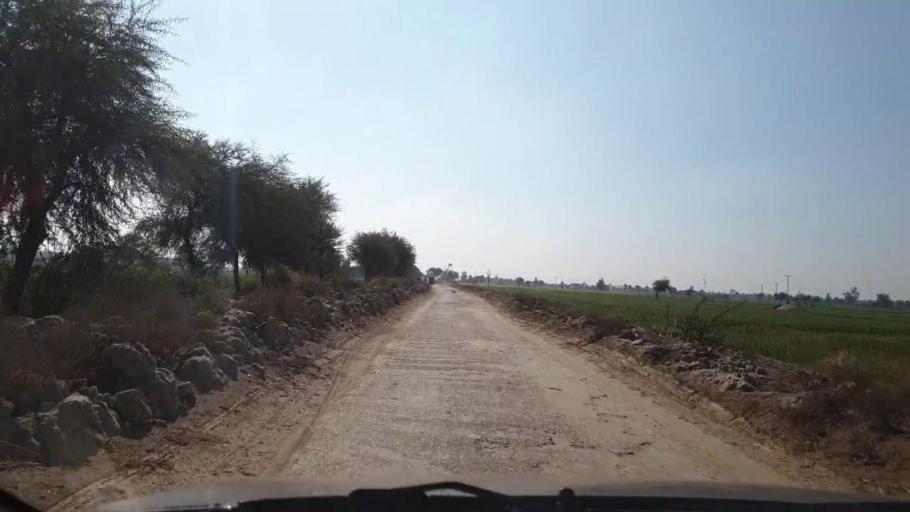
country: PK
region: Sindh
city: Sinjhoro
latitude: 25.9456
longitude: 68.7469
